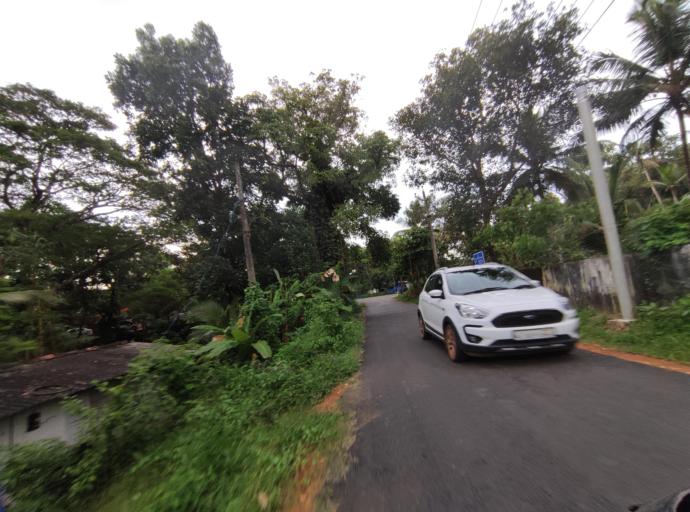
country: IN
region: Kerala
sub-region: Alappuzha
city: Shertallai
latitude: 9.6713
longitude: 76.3336
